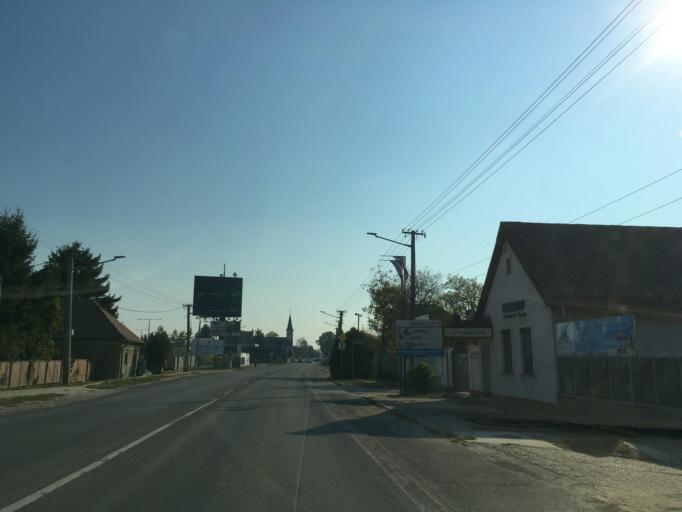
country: SK
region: Bratislavsky
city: Dunajska Luzna
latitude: 48.1042
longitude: 17.2289
